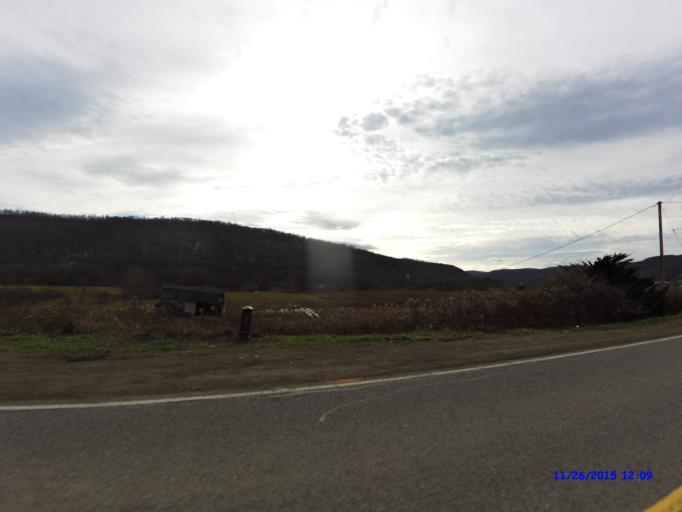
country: US
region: New York
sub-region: Cattaraugus County
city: Allegany
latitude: 42.1928
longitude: -78.4869
